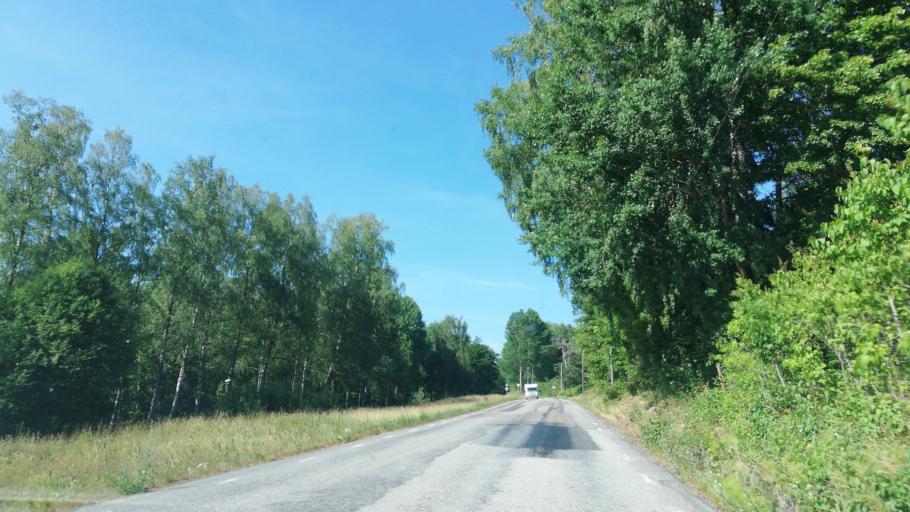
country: SE
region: OEstergoetland
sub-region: Finspangs Kommun
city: Finspang
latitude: 58.7238
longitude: 15.8324
